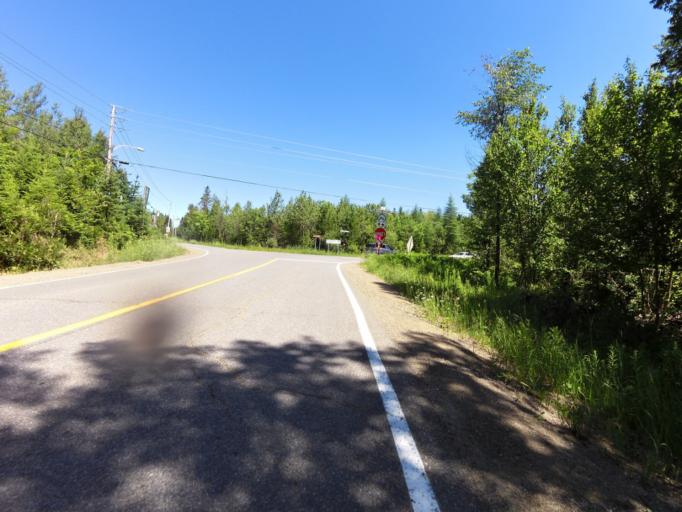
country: CA
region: Quebec
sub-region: Laurentides
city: Brownsburg-Chatham
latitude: 45.8464
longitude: -74.4705
